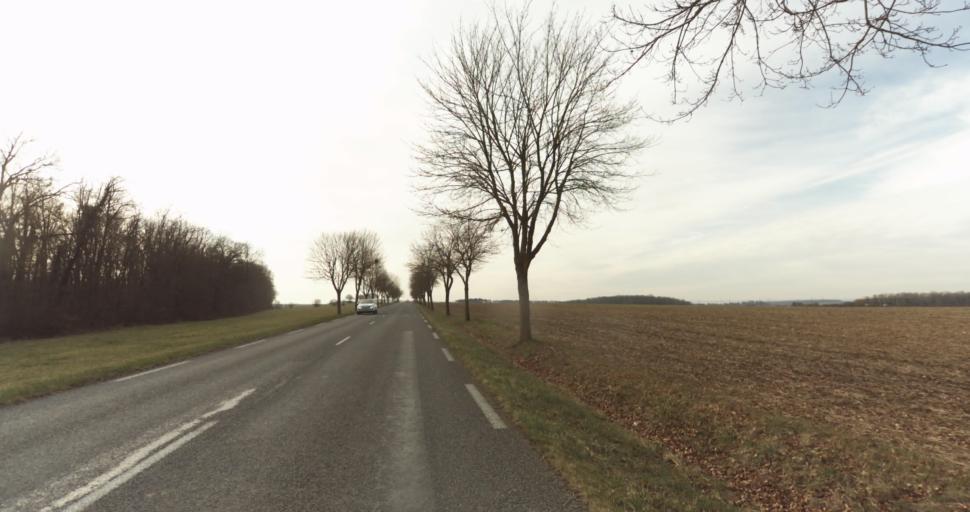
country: FR
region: Lorraine
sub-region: Departement de Meurthe-et-Moselle
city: Jarny
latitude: 49.1324
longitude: 5.8927
